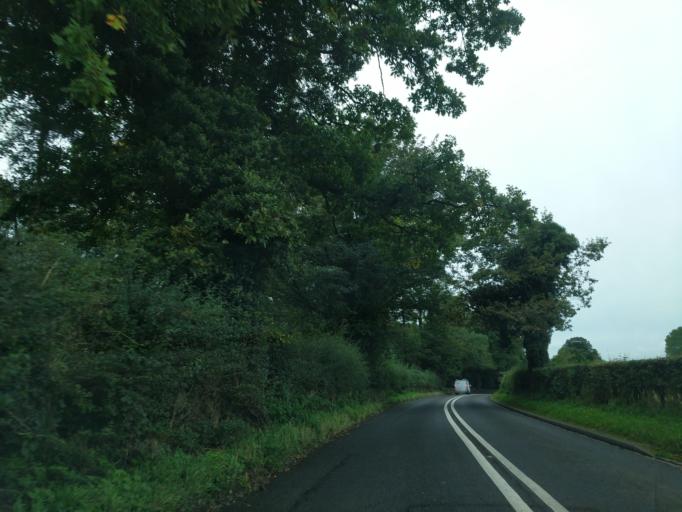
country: GB
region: England
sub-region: Staffordshire
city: Audley
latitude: 53.0143
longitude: -2.3428
